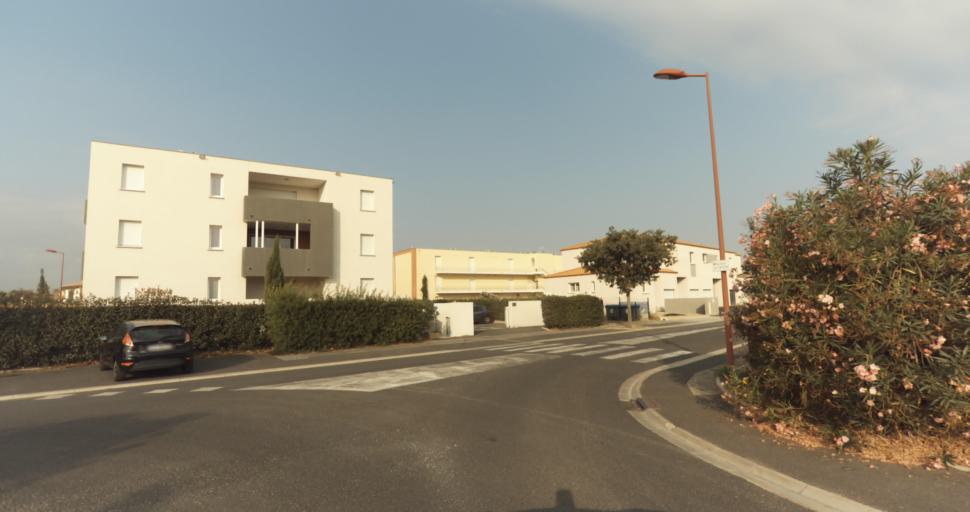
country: FR
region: Languedoc-Roussillon
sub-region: Departement des Pyrenees-Orientales
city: Theza
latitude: 42.6410
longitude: 2.9498
